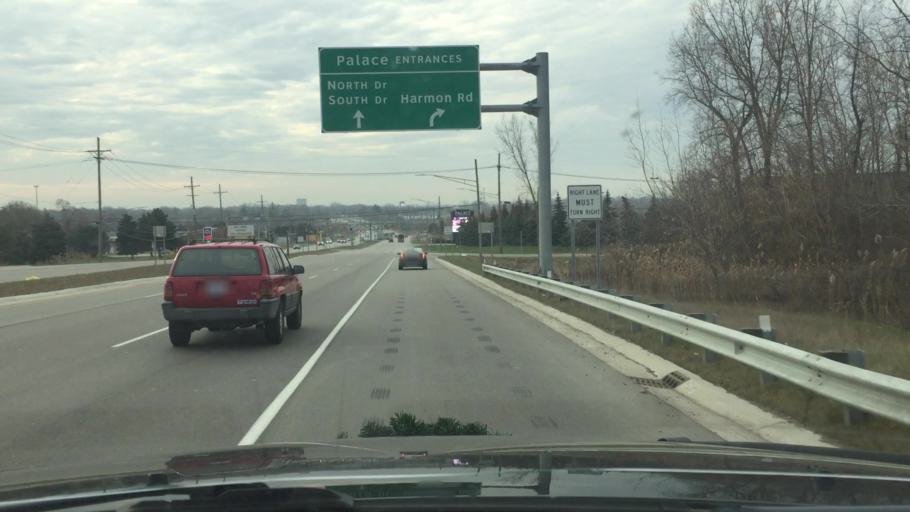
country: US
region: Michigan
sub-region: Oakland County
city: Auburn Hills
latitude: 42.7017
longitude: -83.2426
